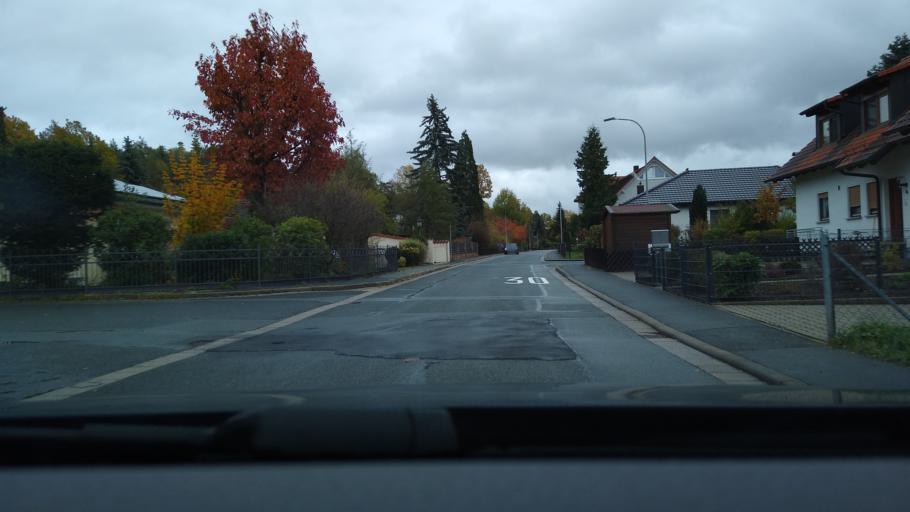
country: DE
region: Bavaria
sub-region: Regierungsbezirk Mittelfranken
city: Hemhofen
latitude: 49.6960
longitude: 10.9350
